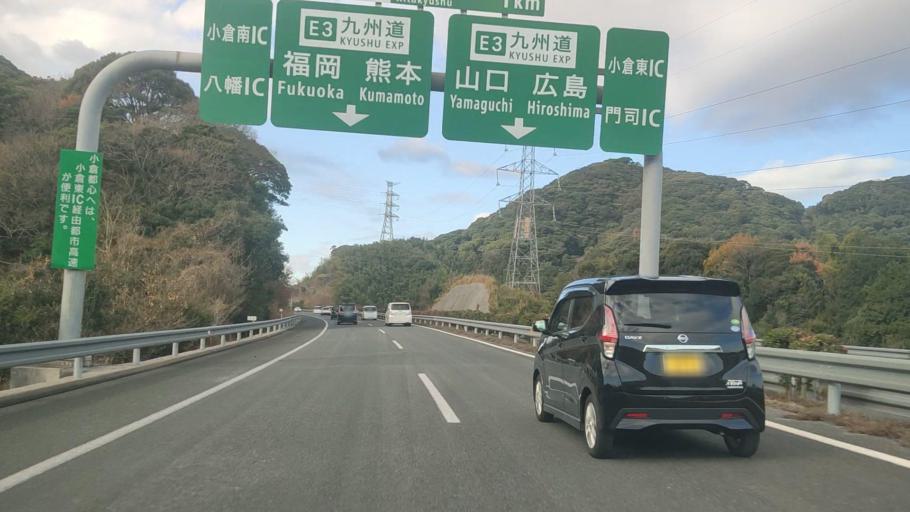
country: JP
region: Fukuoka
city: Kitakyushu
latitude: 33.8156
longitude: 130.8991
